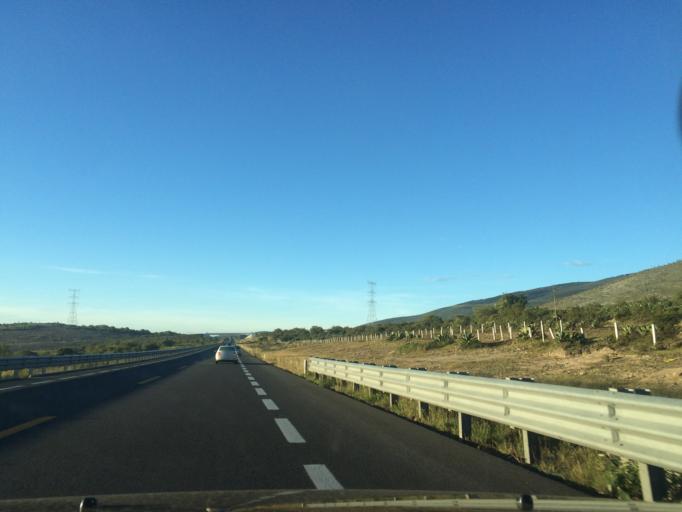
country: MX
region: Puebla
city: Morelos Canada
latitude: 18.7090
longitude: -97.4686
